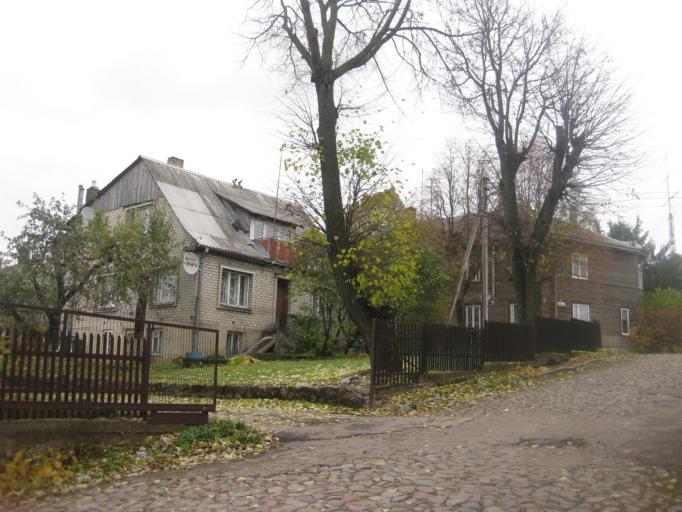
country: LT
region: Kauno apskritis
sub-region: Kaunas
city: Kaunas
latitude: 54.9089
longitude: 23.9106
